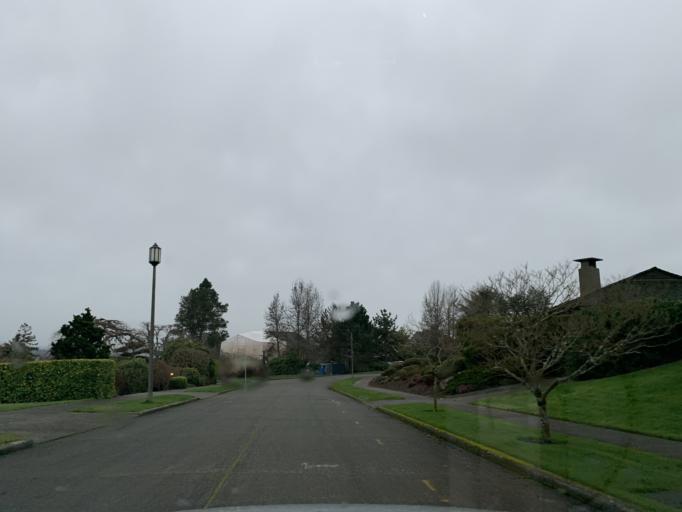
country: US
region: Washington
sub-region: King County
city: Yarrow Point
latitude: 47.6706
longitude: -122.2610
